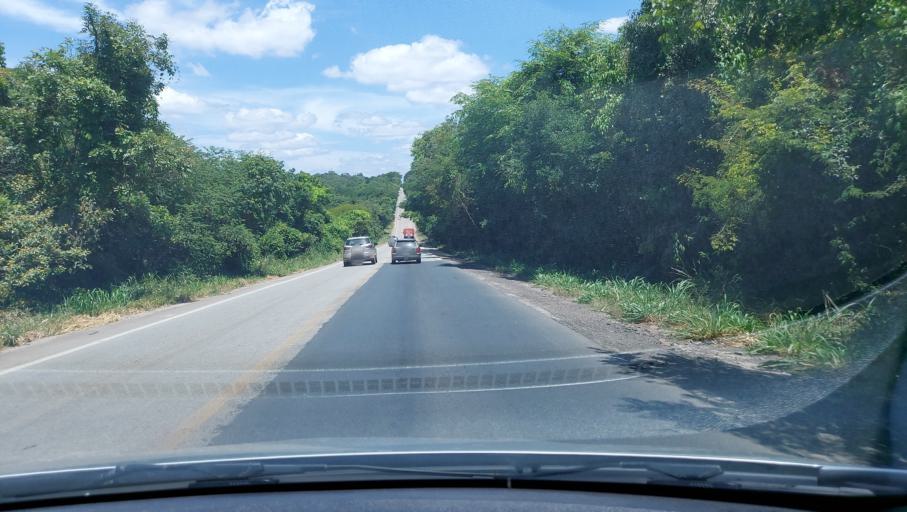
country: BR
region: Bahia
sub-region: Iraquara
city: Iraquara
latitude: -12.4677
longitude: -41.3799
